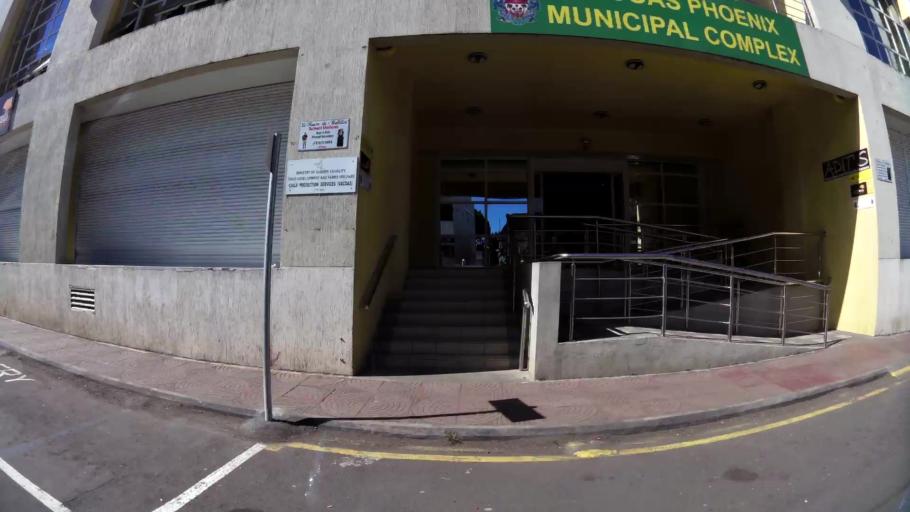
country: MU
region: Plaines Wilhems
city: Vacoas
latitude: -20.2966
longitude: 57.4930
